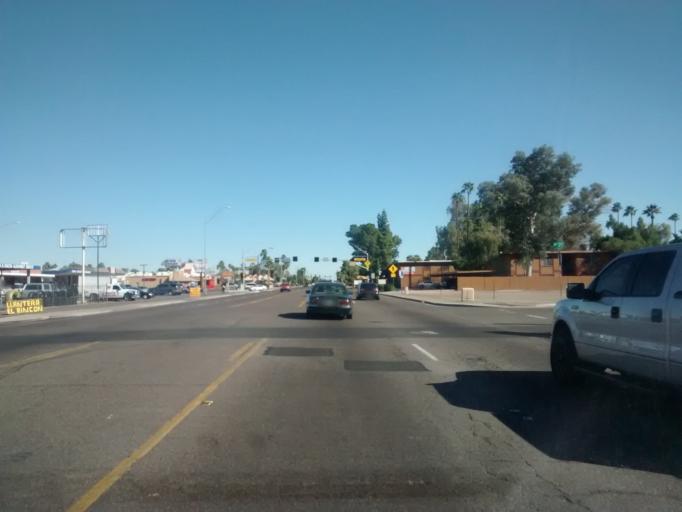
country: US
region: Arizona
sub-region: Maricopa County
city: Glendale
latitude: 33.5241
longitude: -112.1909
